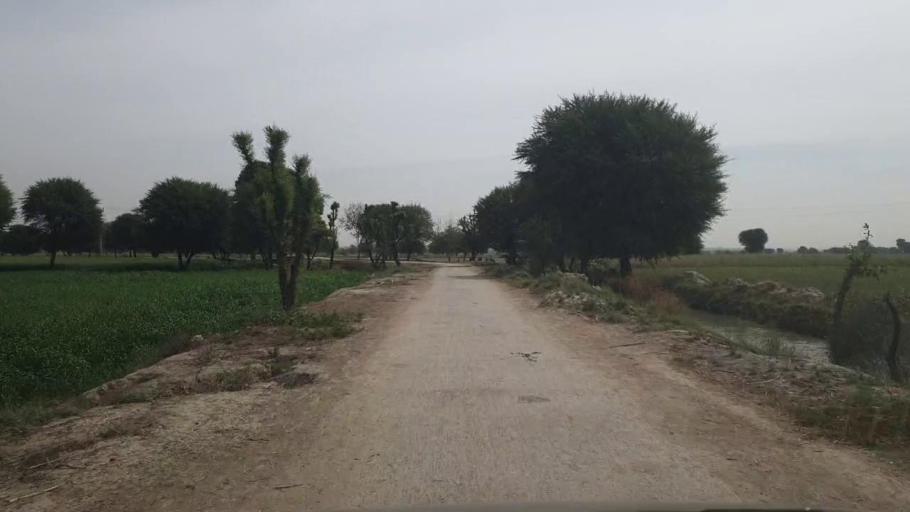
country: PK
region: Sindh
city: Umarkot
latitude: 25.2326
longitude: 69.6978
